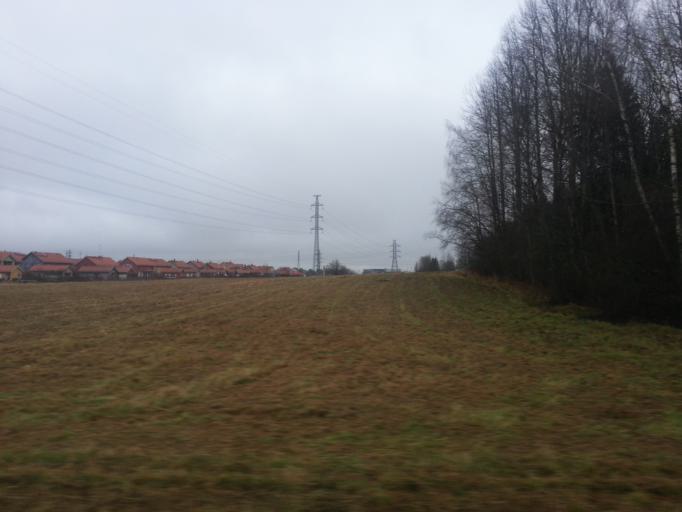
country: FI
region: Uusimaa
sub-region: Helsinki
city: Vantaa
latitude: 60.2783
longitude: 24.9589
